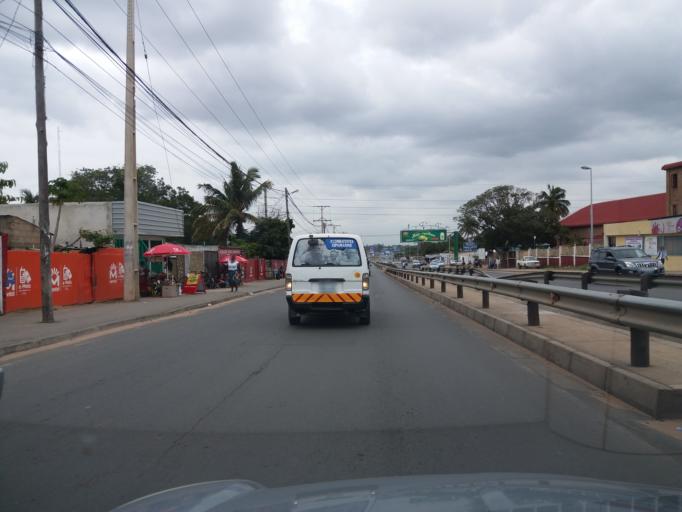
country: MZ
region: Maputo City
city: Maputo
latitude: -25.9511
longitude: 32.5858
